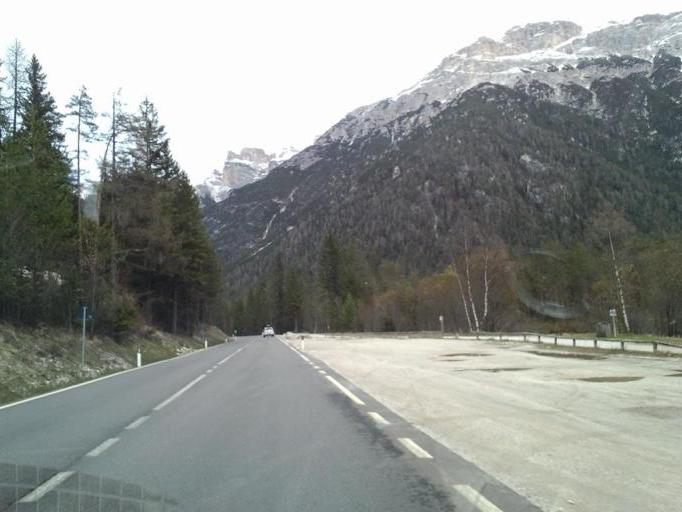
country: IT
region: Trentino-Alto Adige
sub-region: Bolzano
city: Dobbiaco
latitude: 46.6335
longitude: 12.2304
